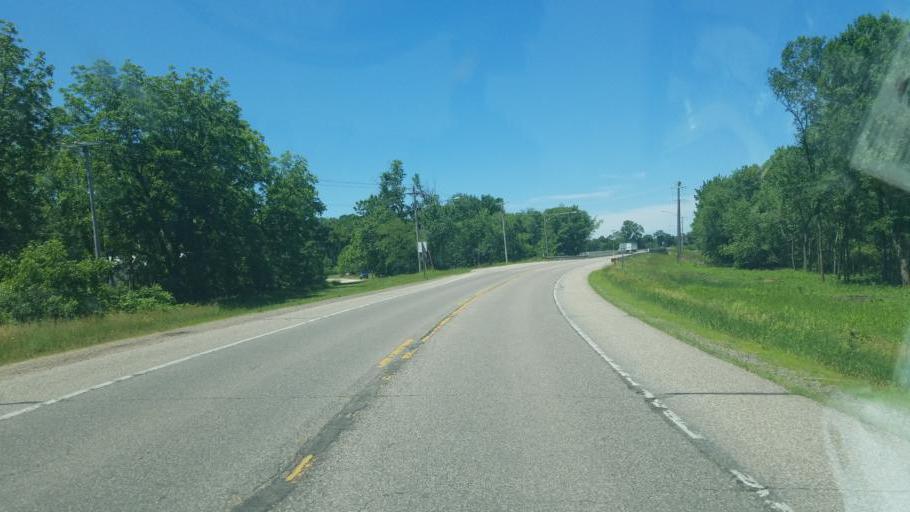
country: US
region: Wisconsin
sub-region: Juneau County
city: New Lisbon
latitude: 44.0273
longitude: -90.0661
